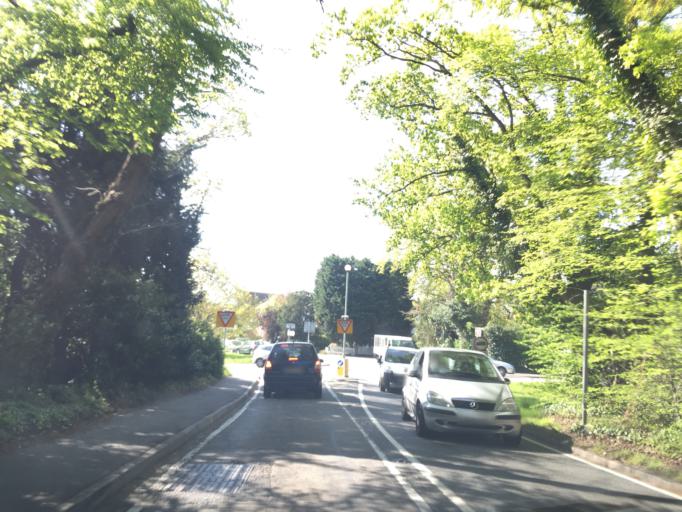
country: GB
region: England
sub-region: Essex
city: Theydon Bois
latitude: 51.6732
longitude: 0.0947
